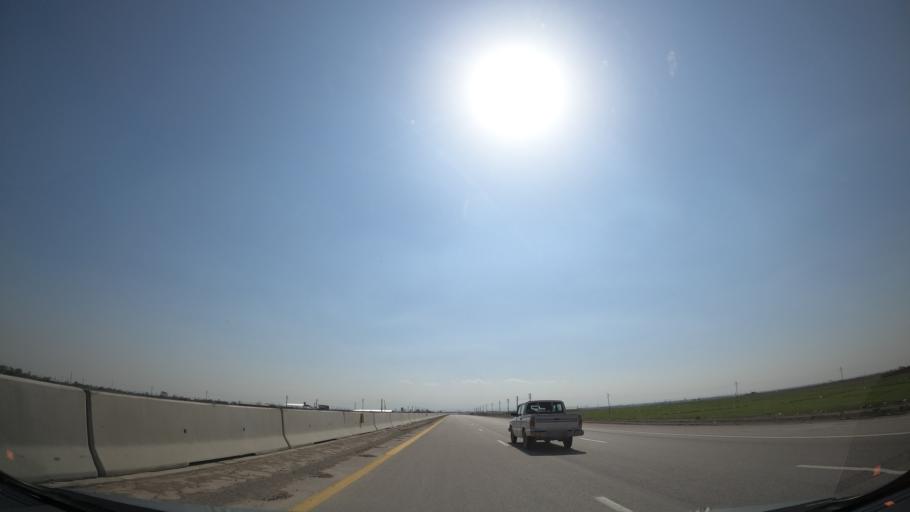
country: IR
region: Qazvin
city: Abyek
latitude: 35.9977
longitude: 50.4618
